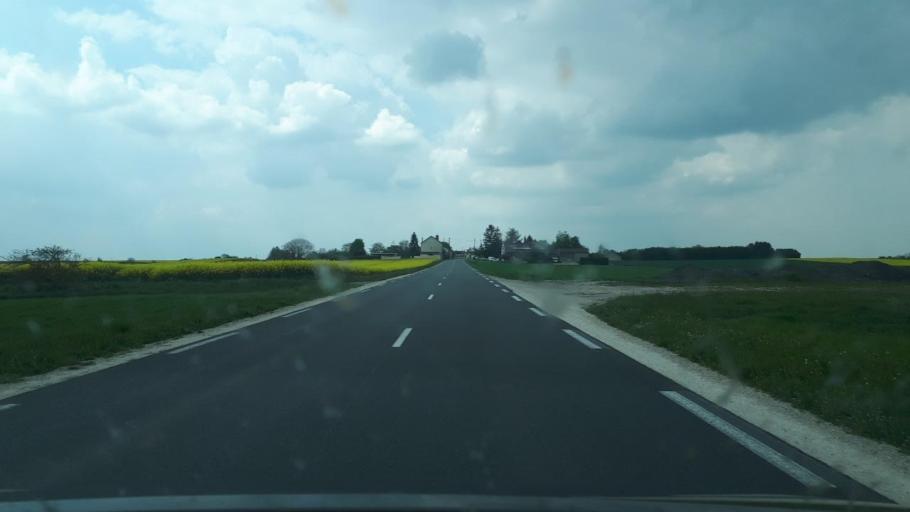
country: FR
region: Centre
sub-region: Departement du Loiret
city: Bazoches-les-Gallerandes
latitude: 48.1633
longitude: 2.1192
